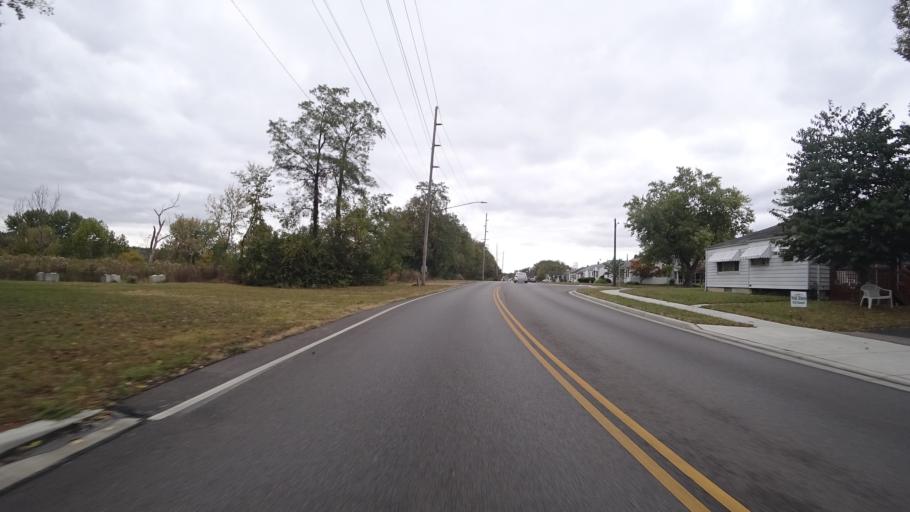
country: US
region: Ohio
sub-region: Butler County
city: Fairfield
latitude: 39.3678
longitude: -84.5635
